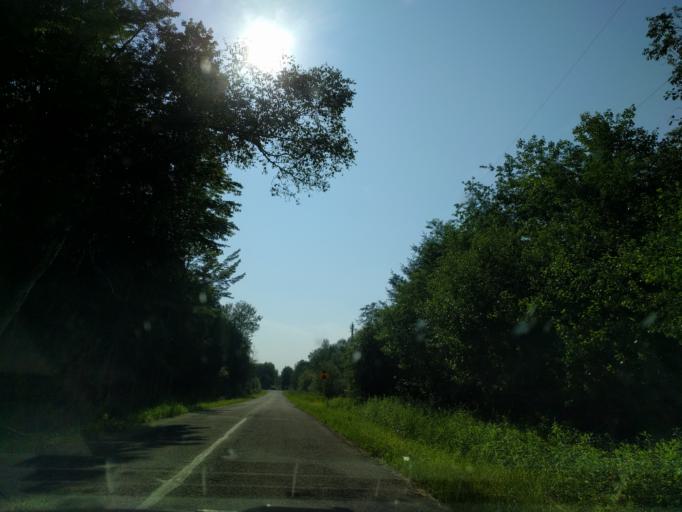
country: US
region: Michigan
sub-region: Delta County
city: Gladstone
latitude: 45.8911
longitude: -87.0622
